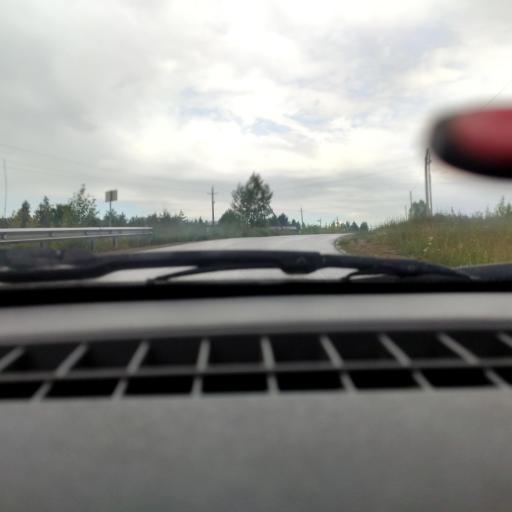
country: RU
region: Bashkortostan
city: Kabakovo
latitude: 54.5665
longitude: 56.2708
